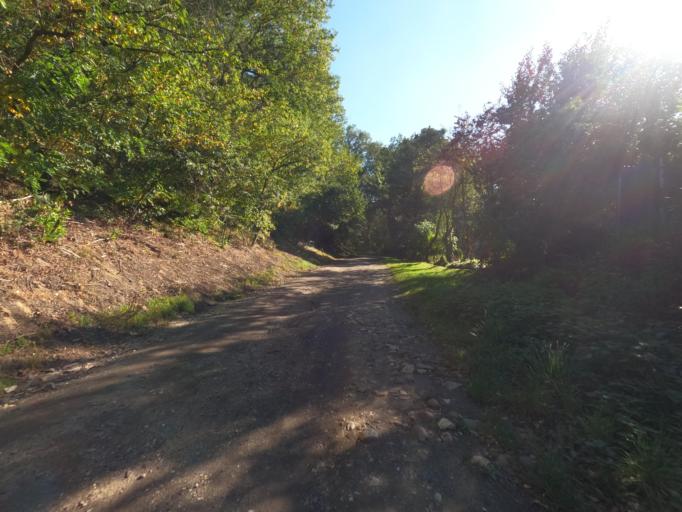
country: DE
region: North Rhine-Westphalia
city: Huckelhoven
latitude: 51.0456
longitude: 6.2527
